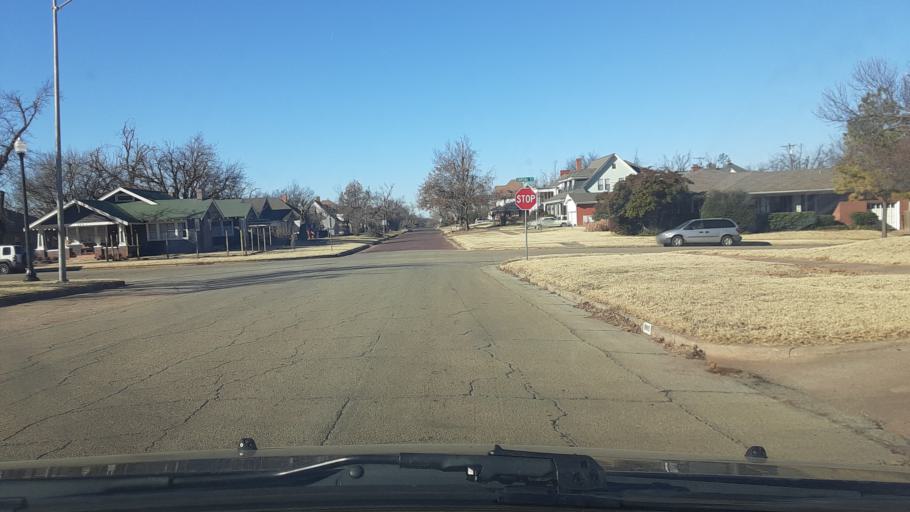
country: US
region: Oklahoma
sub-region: Logan County
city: Guthrie
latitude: 35.8791
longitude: -97.4145
